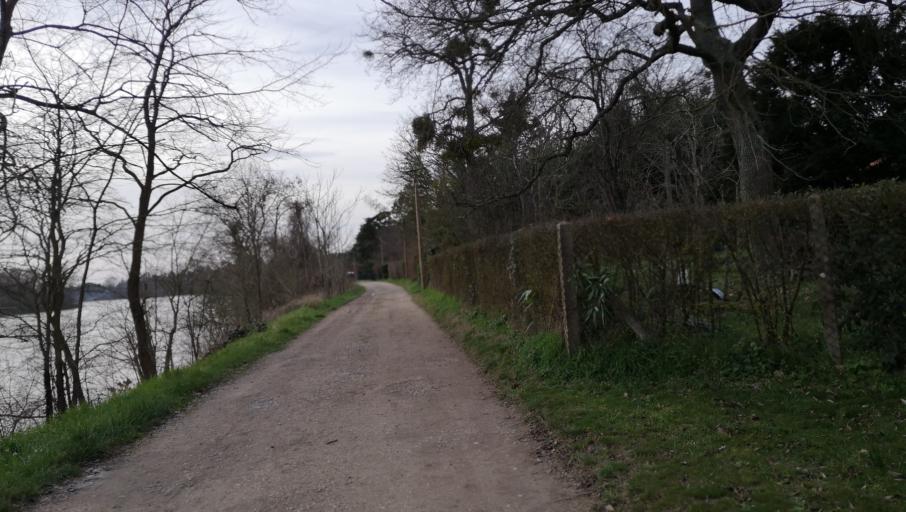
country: FR
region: Centre
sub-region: Departement du Loiret
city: Mareau-aux-Pres
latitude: 47.8667
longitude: 1.7858
